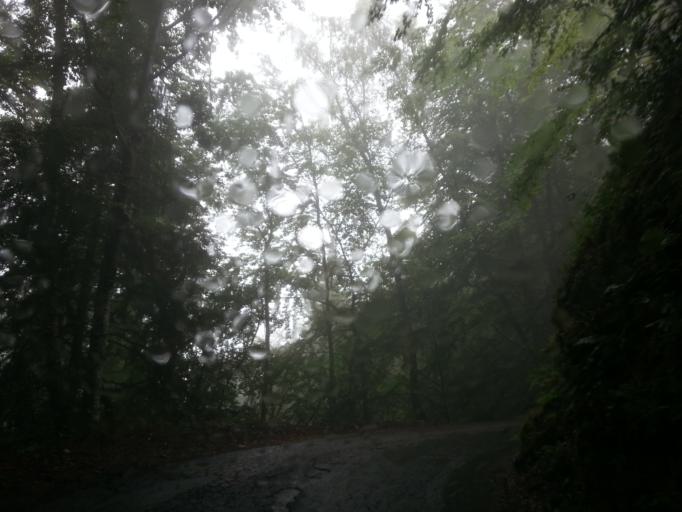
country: FR
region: Rhone-Alpes
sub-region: Departement de la Savoie
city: Albertville
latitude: 45.6778
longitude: 6.4208
